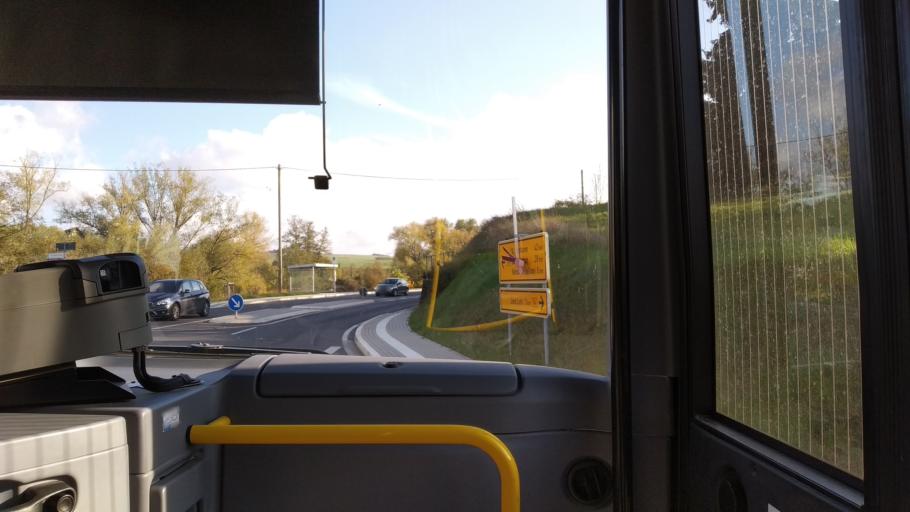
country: DE
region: Rheinland-Pfalz
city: Holzheim
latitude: 50.3514
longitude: 8.0467
